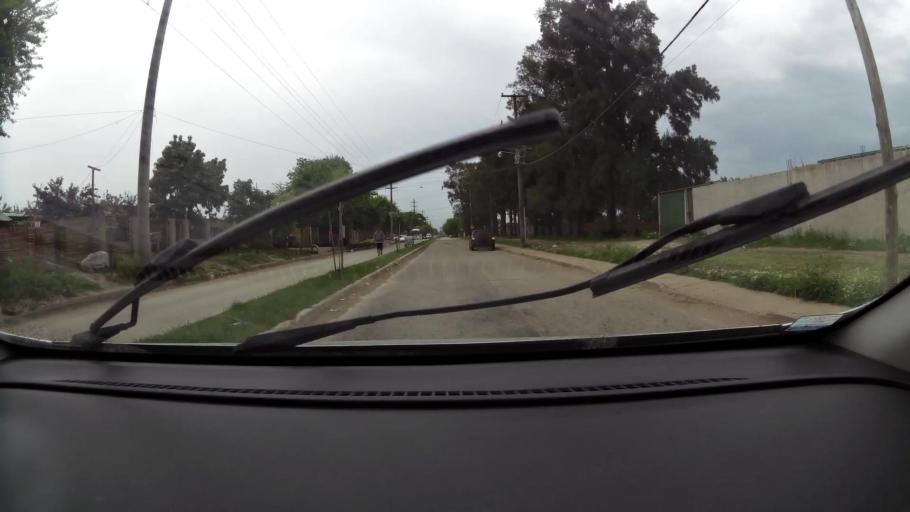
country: AR
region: Buenos Aires
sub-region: Partido de Zarate
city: Zarate
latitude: -34.1119
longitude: -59.0384
